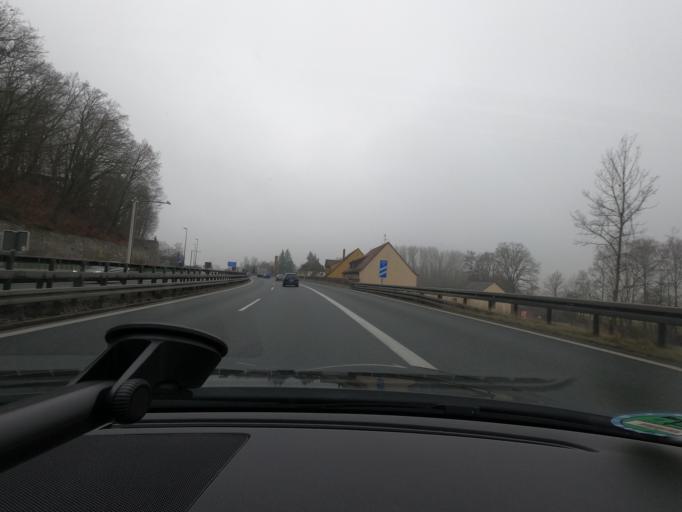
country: DE
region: Bavaria
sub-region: Regierungsbezirk Mittelfranken
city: Mohrendorf
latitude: 49.6112
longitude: 10.9988
